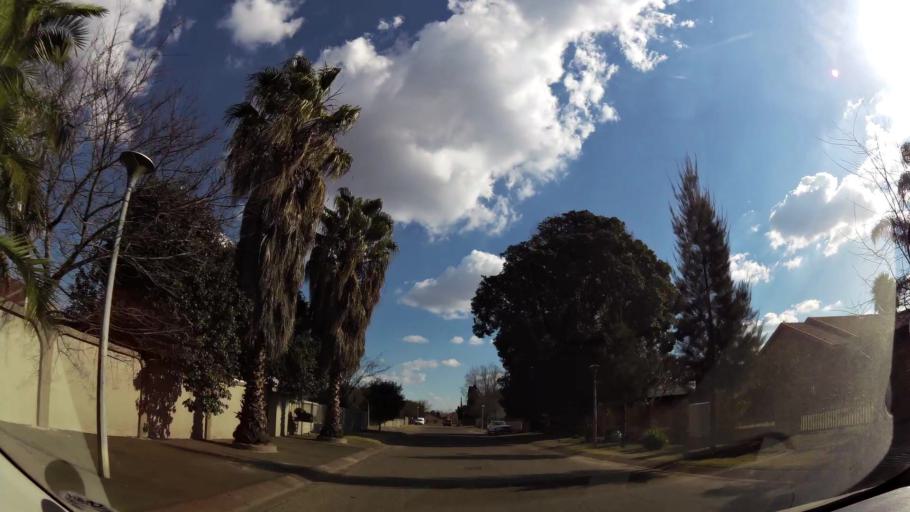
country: ZA
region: Mpumalanga
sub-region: Nkangala District Municipality
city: Witbank
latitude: -25.9171
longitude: 29.2257
